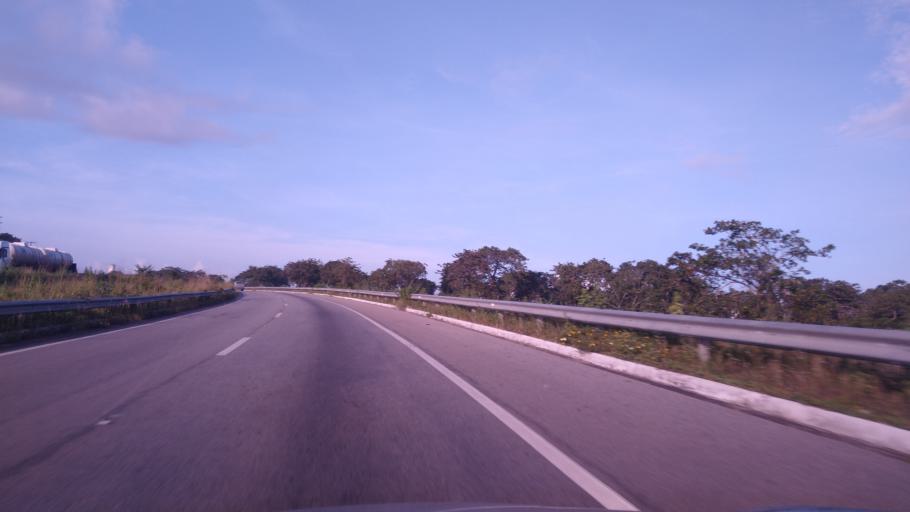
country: BR
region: Ceara
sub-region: Pacajus
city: Pacajus
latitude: -4.1679
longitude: -38.4925
